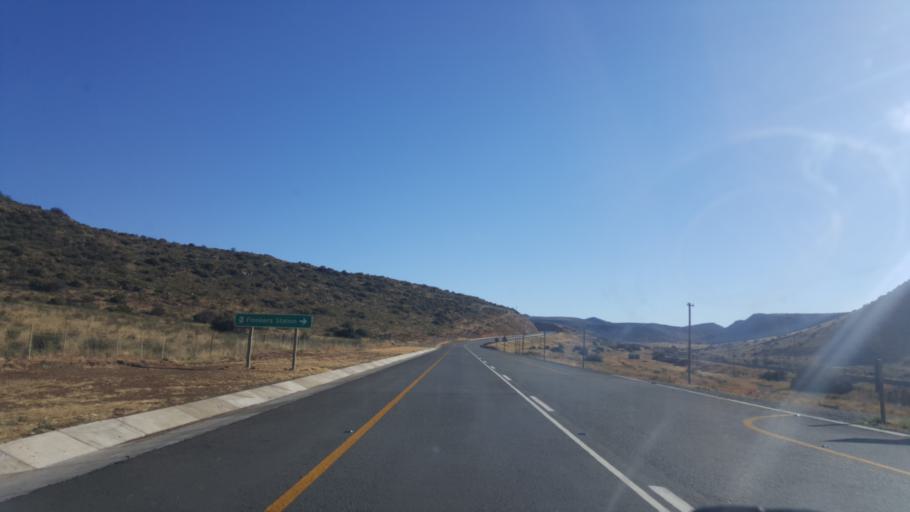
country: ZA
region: Eastern Cape
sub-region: Chris Hani District Municipality
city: Middelburg
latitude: -31.3854
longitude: 25.0316
